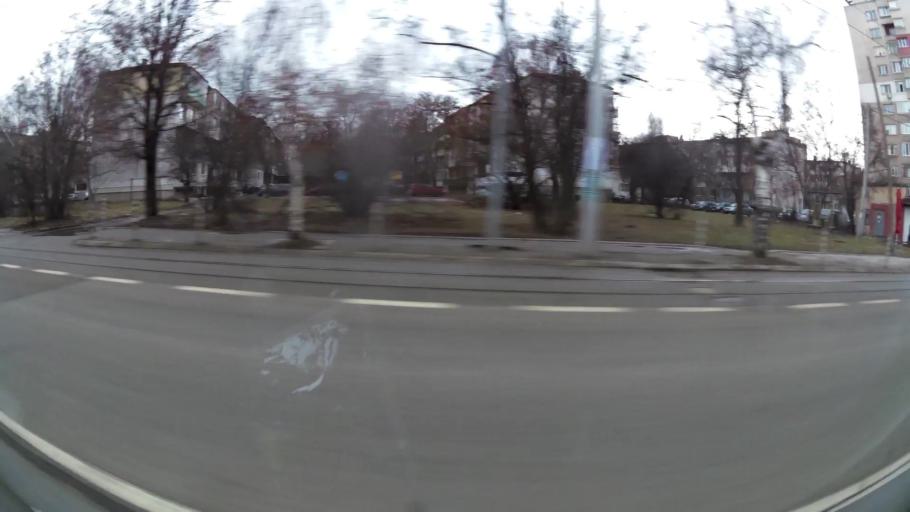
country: BG
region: Sofia-Capital
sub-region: Stolichna Obshtina
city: Sofia
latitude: 42.7370
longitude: 23.3003
